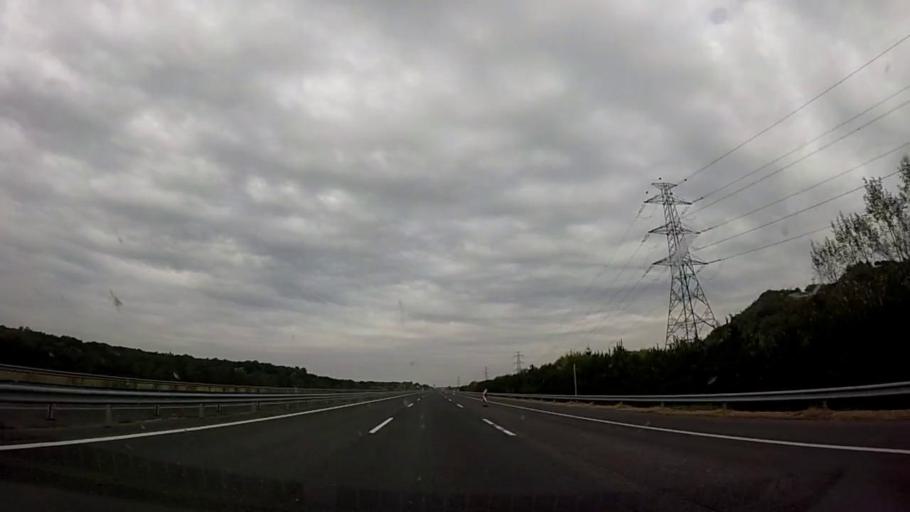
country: HR
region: Medimurska
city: Podturen
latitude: 46.5140
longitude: 16.5411
